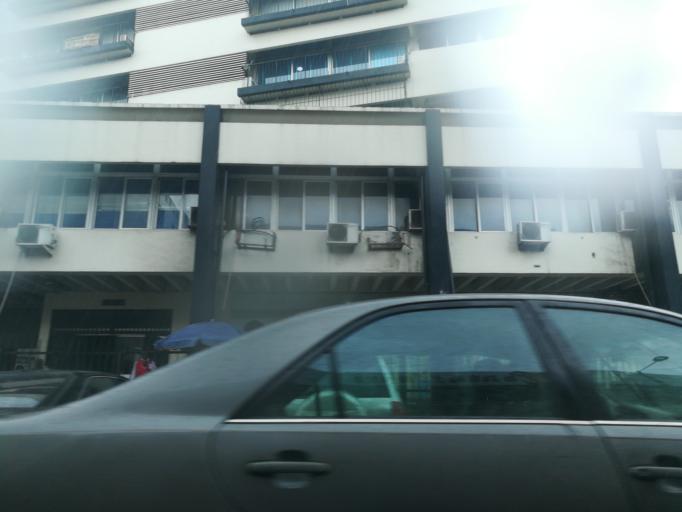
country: NG
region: Lagos
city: Lagos
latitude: 6.4515
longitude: 3.3905
